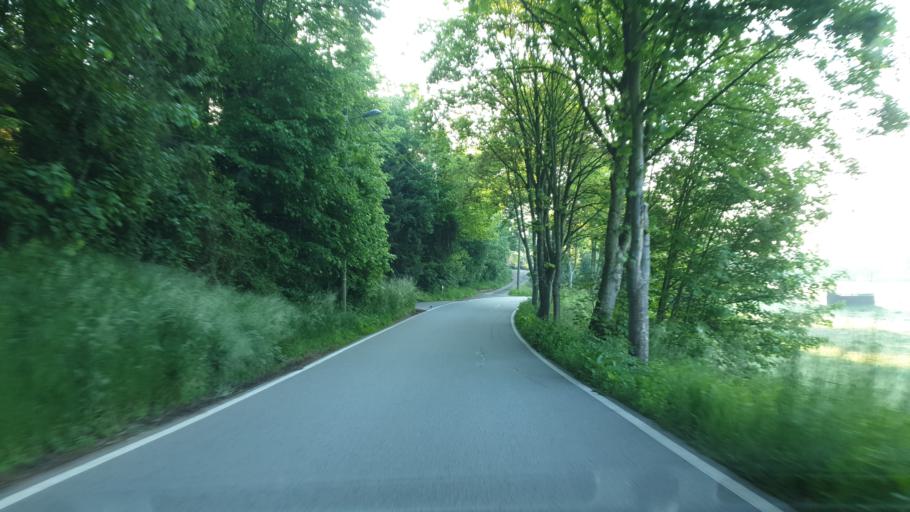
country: DE
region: Saxony
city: Bernsdorf
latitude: 50.7865
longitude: 12.6557
